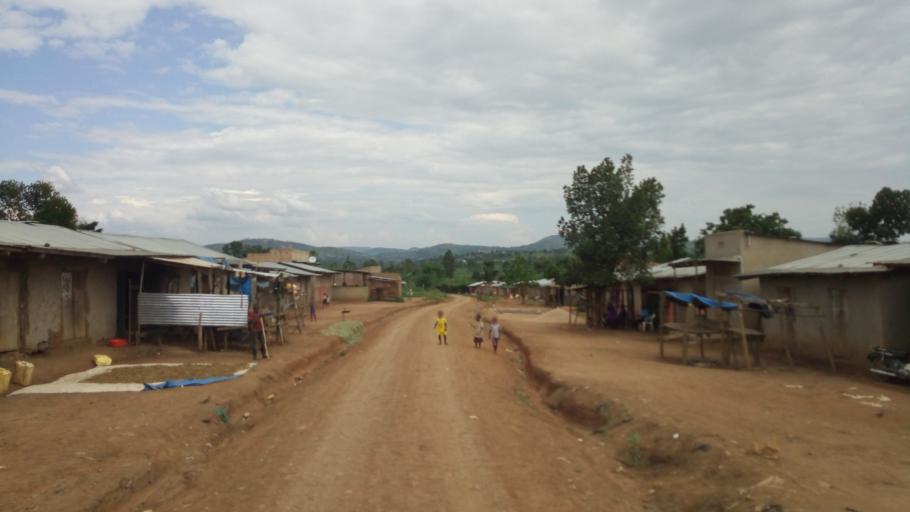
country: UG
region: Central Region
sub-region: Kiboga District
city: Kiboga
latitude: 0.7621
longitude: 31.6896
